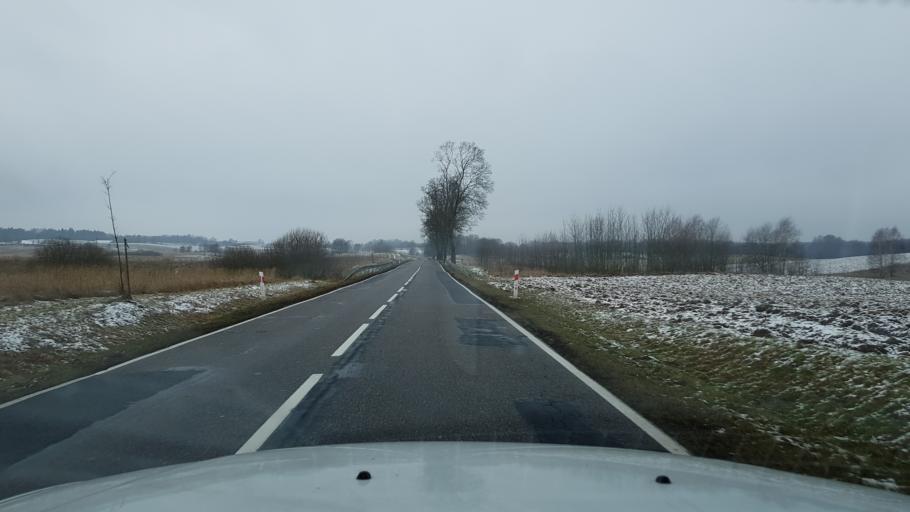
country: PL
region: West Pomeranian Voivodeship
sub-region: Powiat drawski
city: Czaplinek
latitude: 53.5613
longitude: 16.1623
